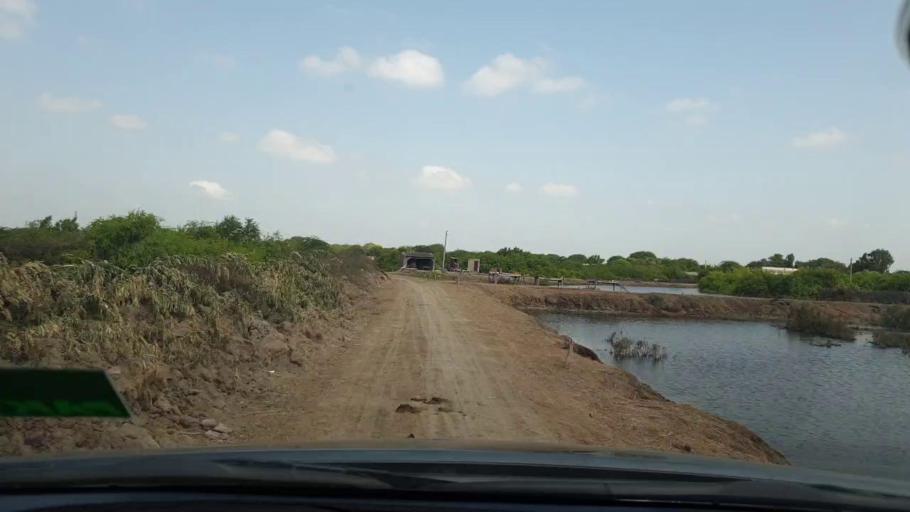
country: PK
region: Sindh
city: Tando Bago
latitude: 24.9551
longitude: 69.0755
